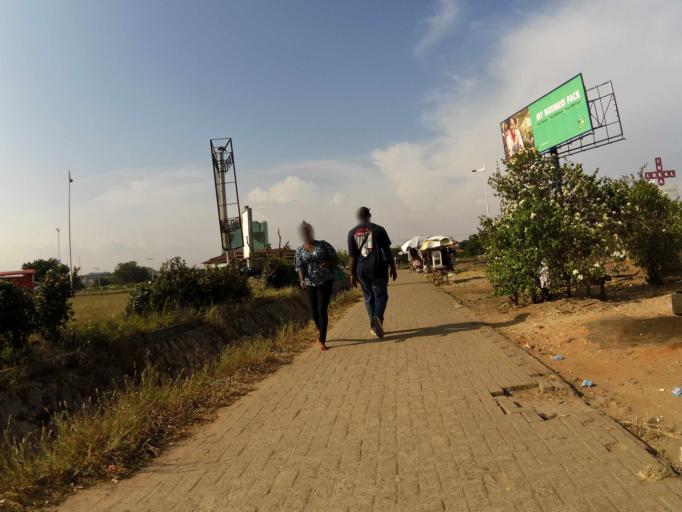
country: GH
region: Greater Accra
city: Medina Estates
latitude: 5.6232
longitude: -0.1739
